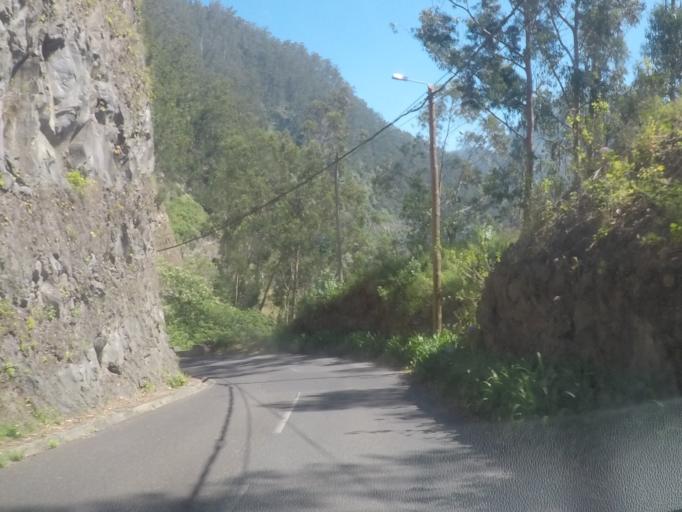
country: PT
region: Madeira
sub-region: Camara de Lobos
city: Curral das Freiras
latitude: 32.6884
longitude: -16.9707
